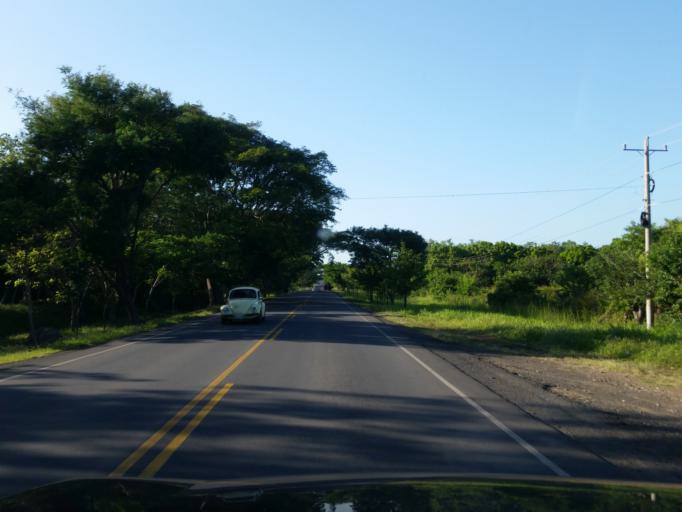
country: NI
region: Rivas
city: Rivas
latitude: 11.3965
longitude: -85.7770
